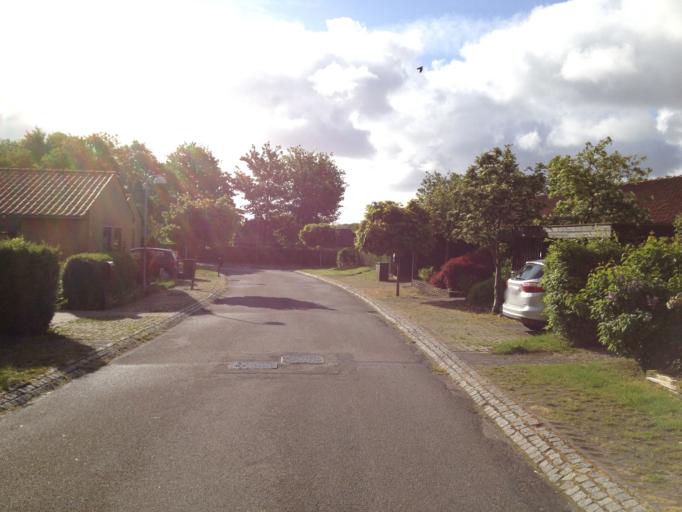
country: DK
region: Capital Region
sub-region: Fredensborg Kommune
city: Niva
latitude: 55.9331
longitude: 12.4998
